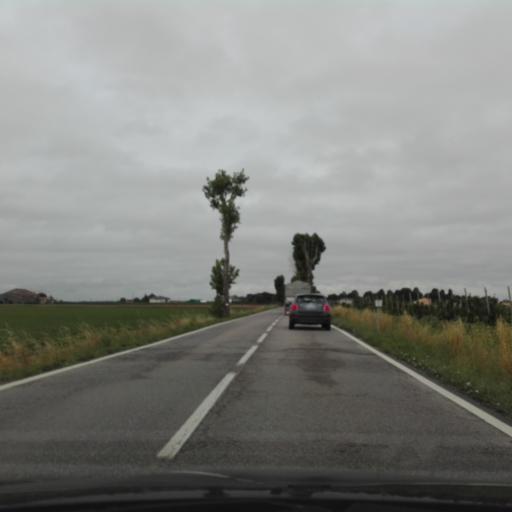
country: IT
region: Veneto
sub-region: Provincia di Rovigo
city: Lusia
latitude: 45.0753
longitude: 11.6670
